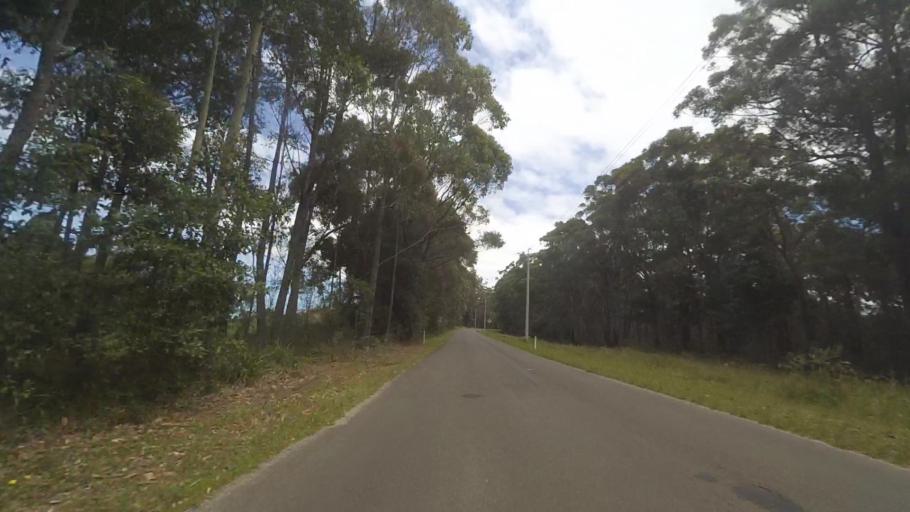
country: AU
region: New South Wales
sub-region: Shoalhaven Shire
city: Milton
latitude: -35.3802
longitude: 150.3729
